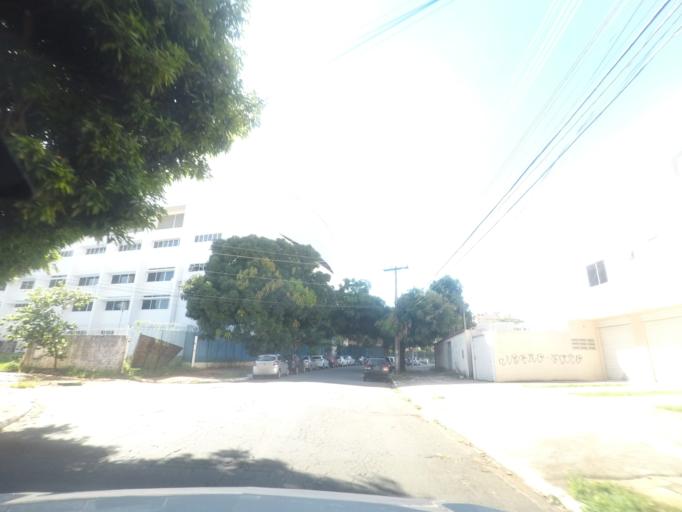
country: BR
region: Goias
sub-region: Goiania
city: Goiania
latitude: -16.6710
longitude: -49.2643
